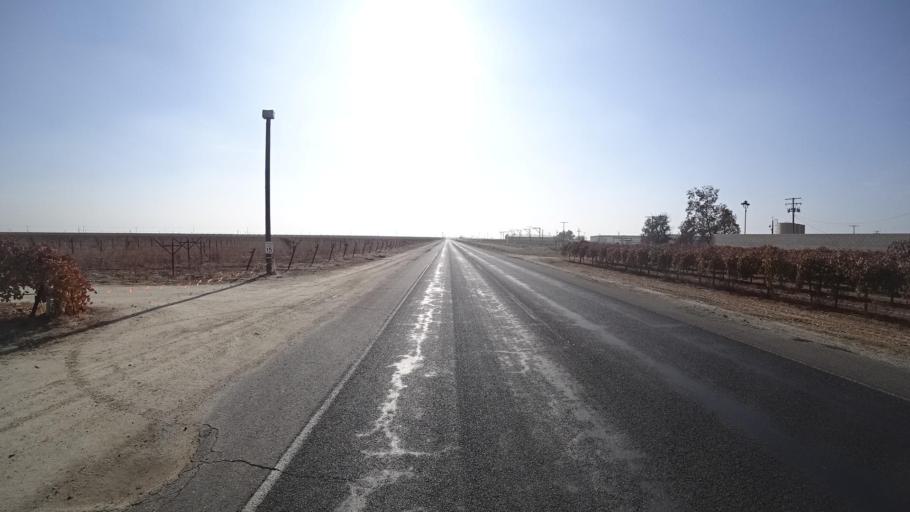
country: US
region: California
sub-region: Kern County
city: McFarland
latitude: 35.6783
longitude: -119.1842
